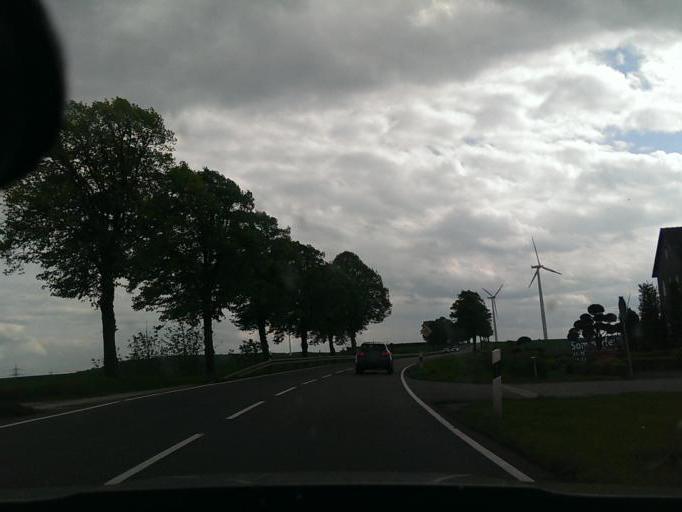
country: DE
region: Lower Saxony
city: Nordstemmen
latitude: 52.2028
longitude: 9.7478
